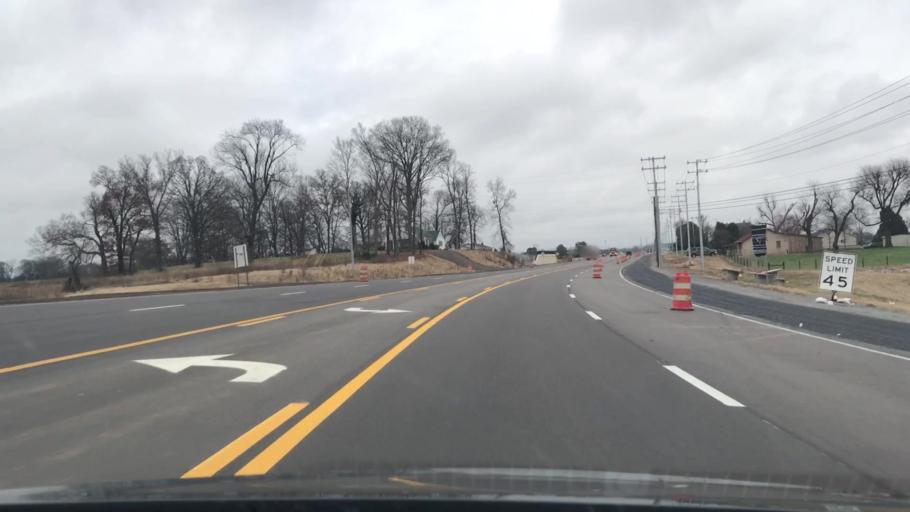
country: US
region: Tennessee
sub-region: Montgomery County
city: Clarksville
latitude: 36.6073
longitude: -87.2741
